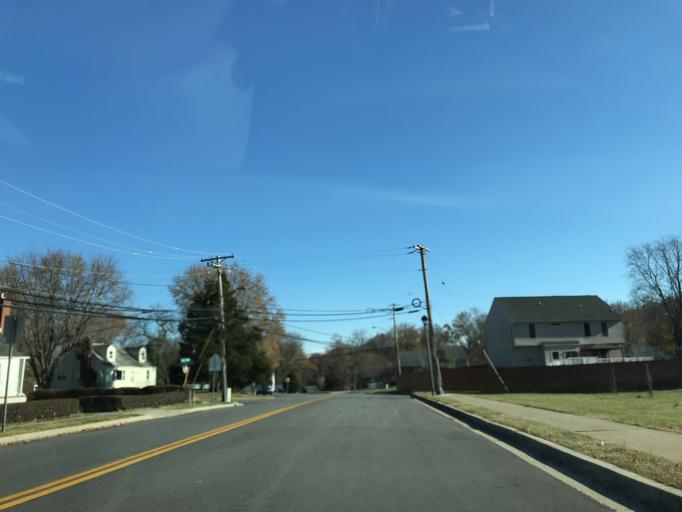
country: US
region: Maryland
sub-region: Baltimore County
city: Bowleys Quarters
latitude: 39.3714
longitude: -76.3533
